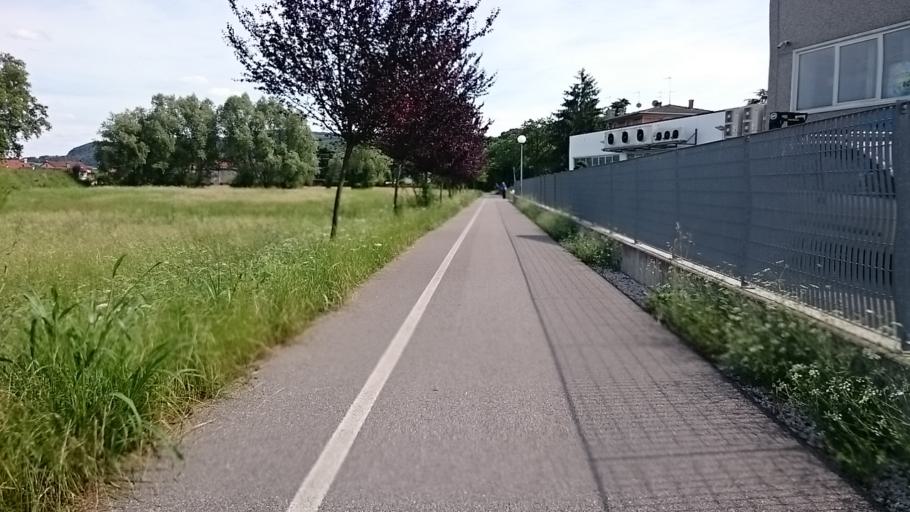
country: IT
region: Veneto
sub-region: Provincia di Vicenza
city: Arcugnano-Torri
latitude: 45.5077
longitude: 11.5701
